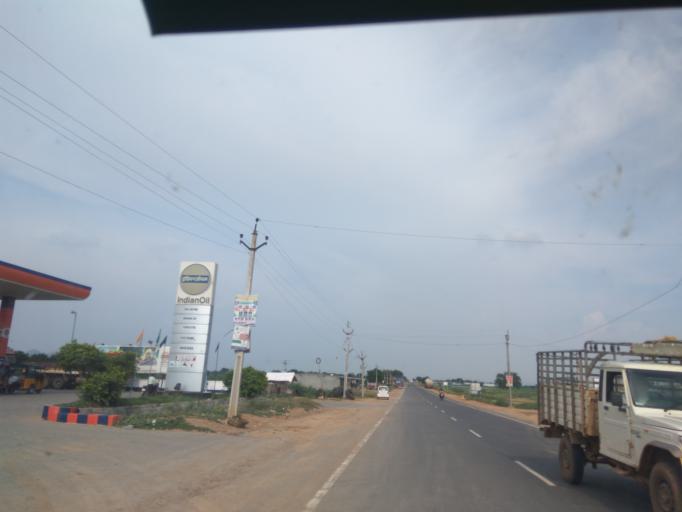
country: IN
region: Andhra Pradesh
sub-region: Prakasam
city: Chemmumiahpet
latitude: 15.9021
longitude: 79.3015
